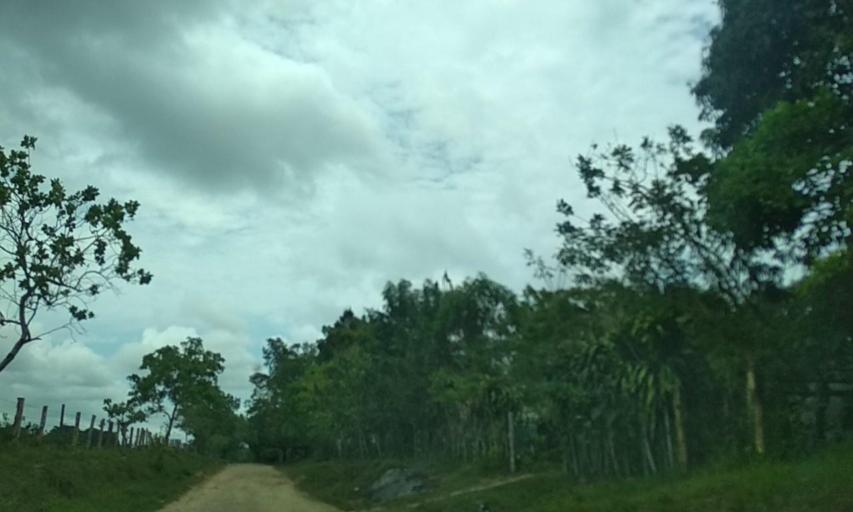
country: MX
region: Veracruz
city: Las Choapas
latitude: 17.8925
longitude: -94.1161
